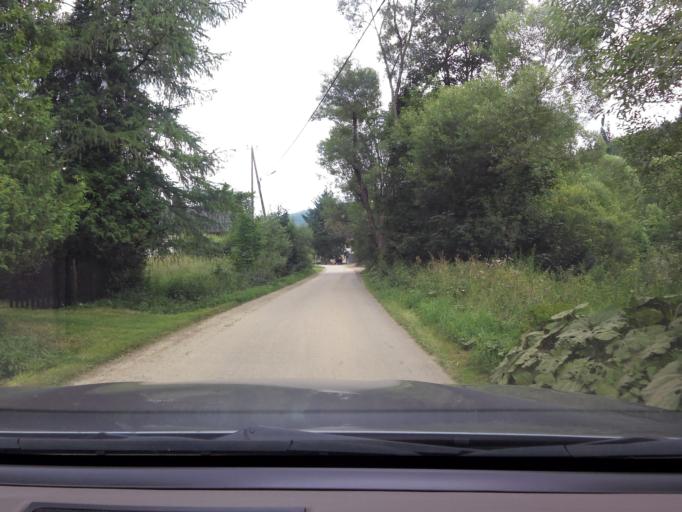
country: PL
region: Silesian Voivodeship
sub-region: Powiat zywiecki
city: Ujsoly
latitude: 49.5056
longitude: 19.1405
